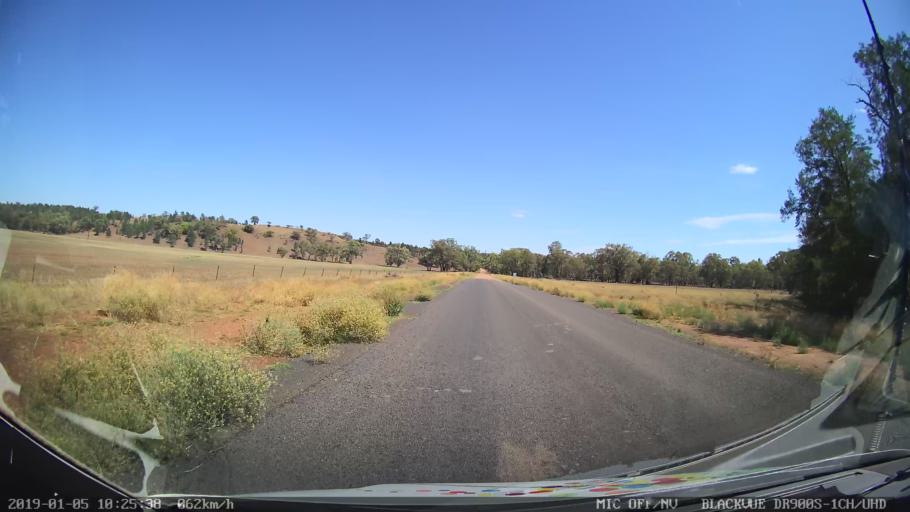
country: AU
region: New South Wales
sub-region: Gilgandra
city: Gilgandra
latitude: -31.5597
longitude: 148.9584
